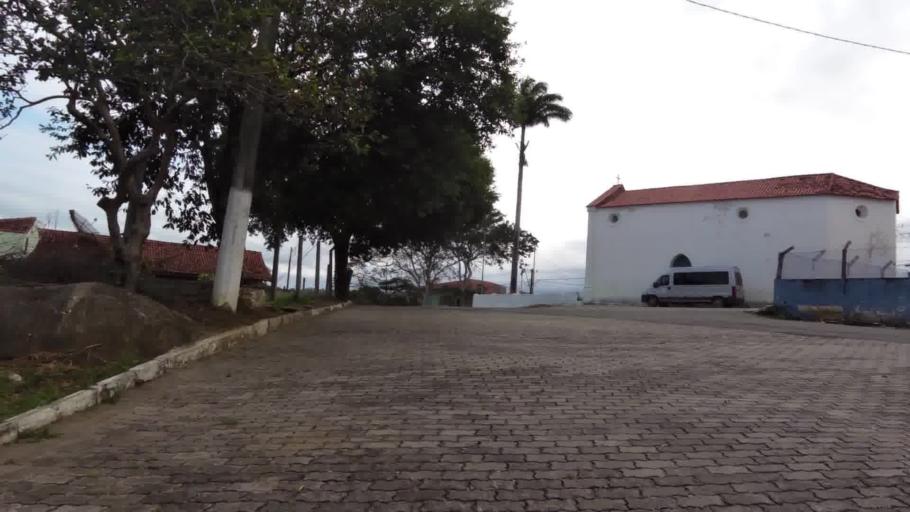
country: BR
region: Espirito Santo
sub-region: Piuma
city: Piuma
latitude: -20.8033
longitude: -40.6527
